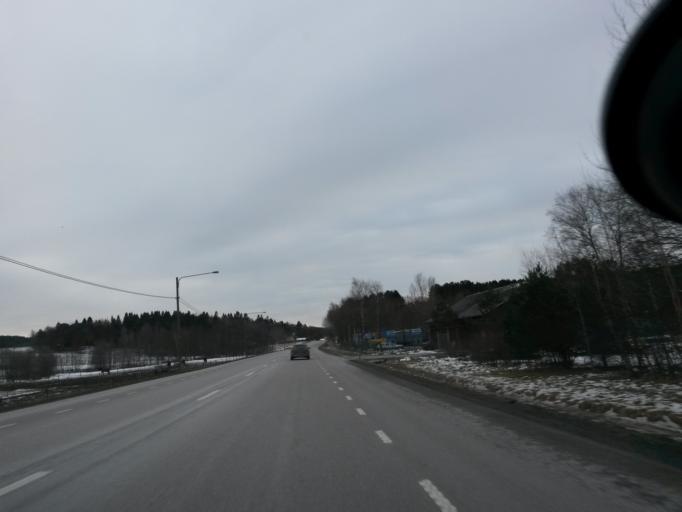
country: SE
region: Vaestra Goetaland
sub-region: Alingsas Kommun
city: Alingsas
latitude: 57.9484
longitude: 12.6000
